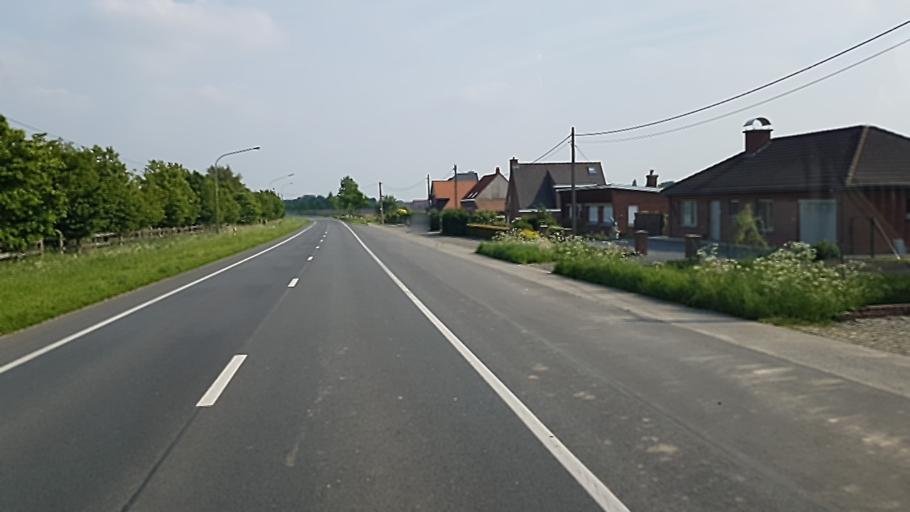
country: BE
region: Flanders
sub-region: Provincie West-Vlaanderen
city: Zwevegem
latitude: 50.7531
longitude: 3.3149
